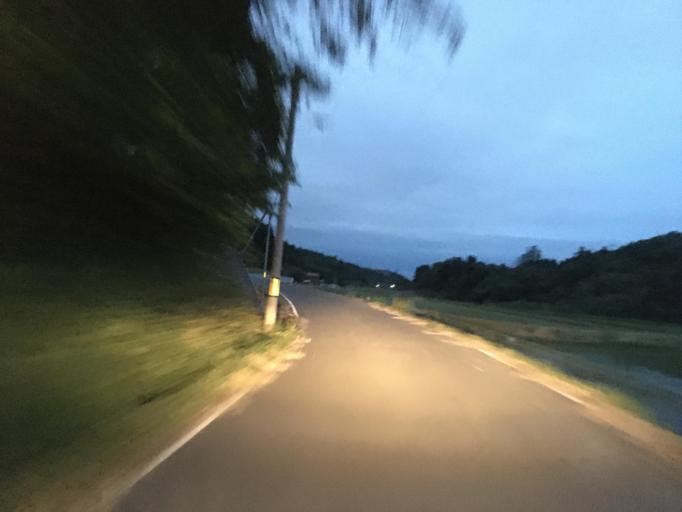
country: JP
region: Miyagi
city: Furukawa
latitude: 38.7864
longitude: 140.9332
